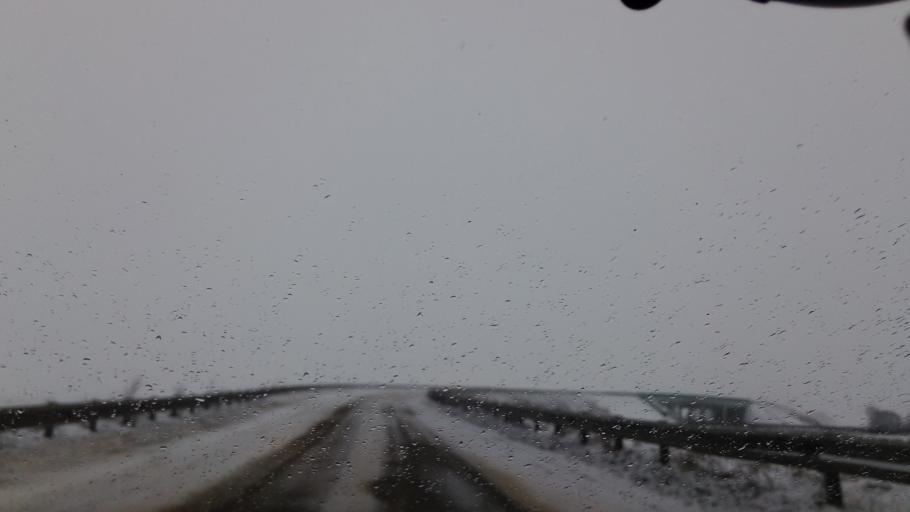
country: RU
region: Tula
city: Bogoroditsk
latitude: 53.7075
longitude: 38.0440
